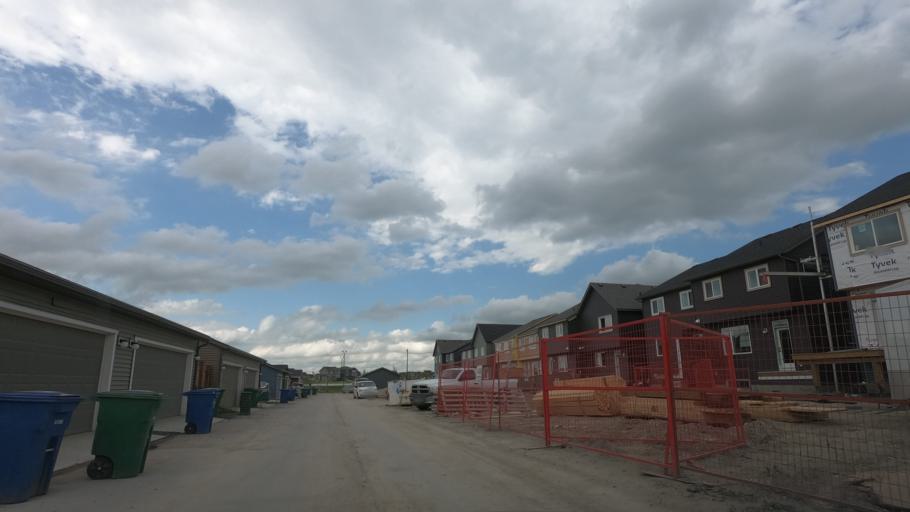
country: CA
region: Alberta
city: Airdrie
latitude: 51.2580
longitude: -113.9823
